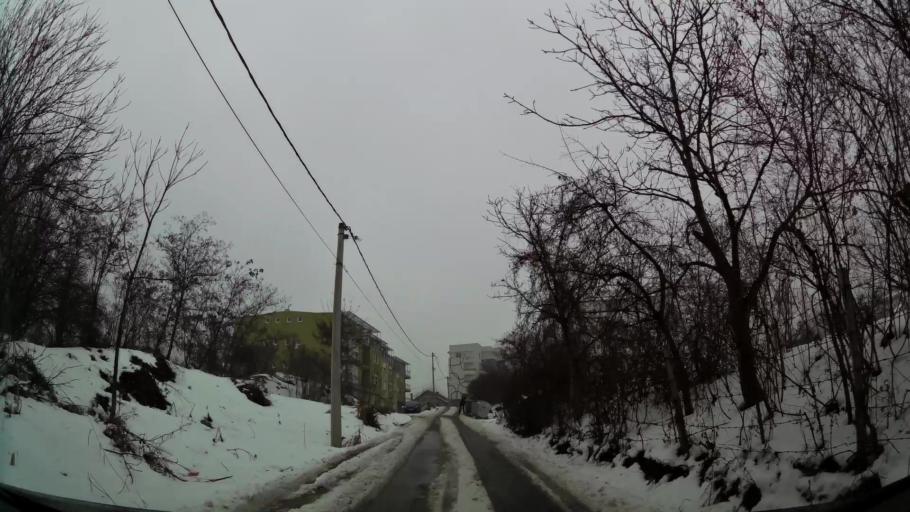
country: RS
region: Central Serbia
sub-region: Belgrade
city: Zvezdara
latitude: 44.7851
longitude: 20.5307
